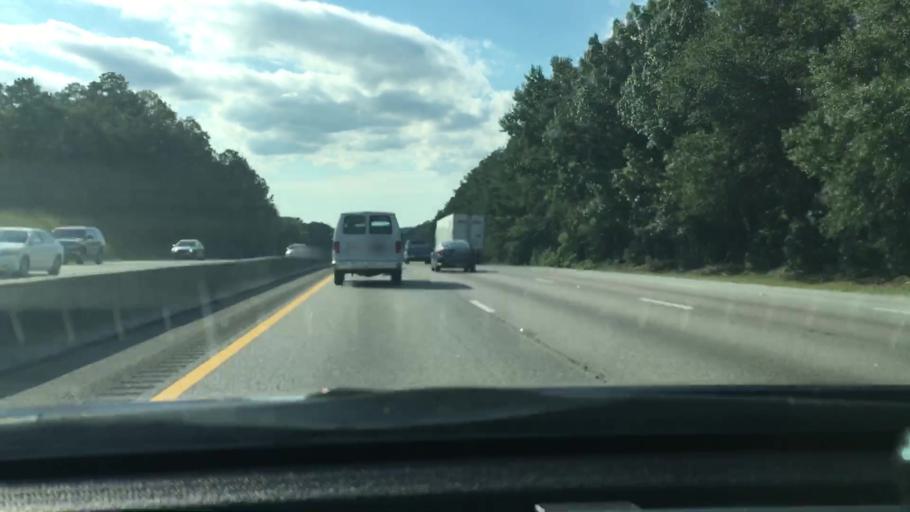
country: US
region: South Carolina
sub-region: Richland County
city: Forest Acres
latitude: 34.0662
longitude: -81.0273
